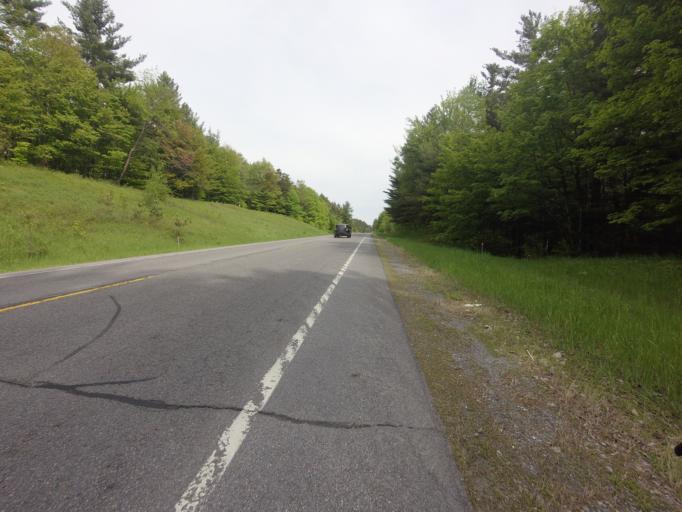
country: US
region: New York
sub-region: St. Lawrence County
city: Gouverneur
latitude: 44.2875
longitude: -75.2118
